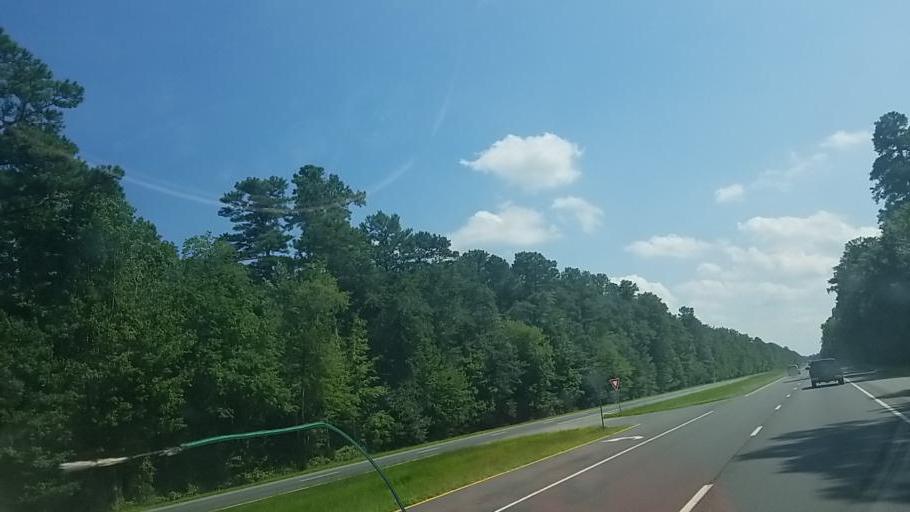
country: US
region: Delaware
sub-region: Sussex County
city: Georgetown
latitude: 38.7806
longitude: -75.4387
